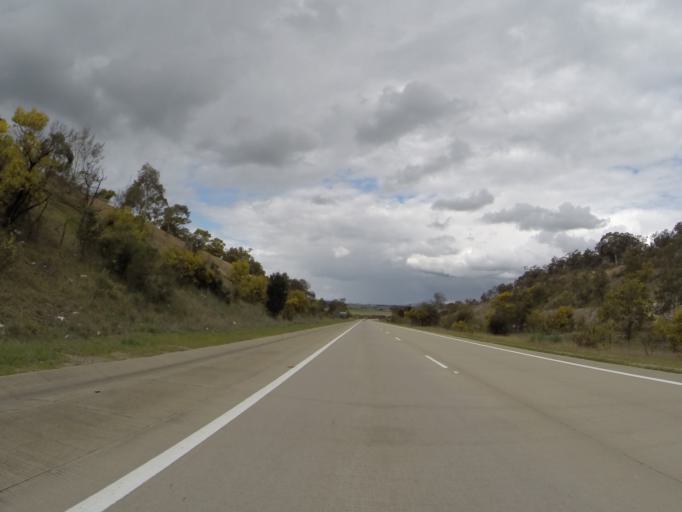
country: AU
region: New South Wales
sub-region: Goulburn Mulwaree
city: Goulburn
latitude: -34.8025
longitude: 149.5024
